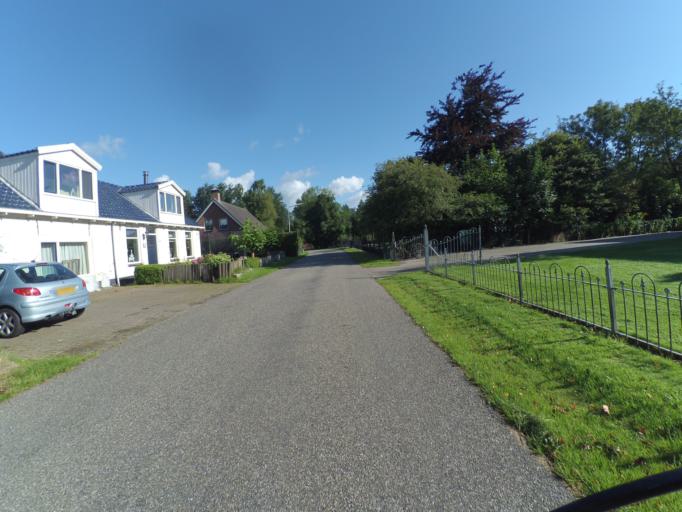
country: NL
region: Friesland
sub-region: Gemeente Kollumerland en Nieuwkruisland
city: Kollumerzwaag
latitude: 53.2767
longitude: 6.0897
